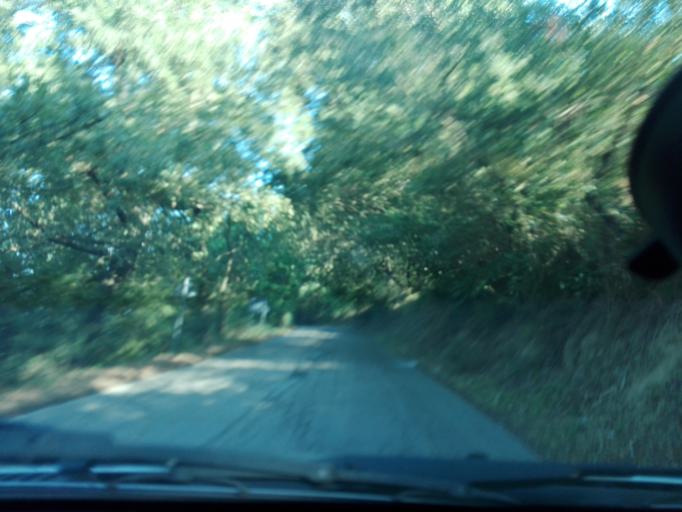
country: IT
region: Abruzzo
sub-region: Provincia di Pescara
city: Cappelle sul Tavo
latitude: 42.4500
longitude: 14.0887
